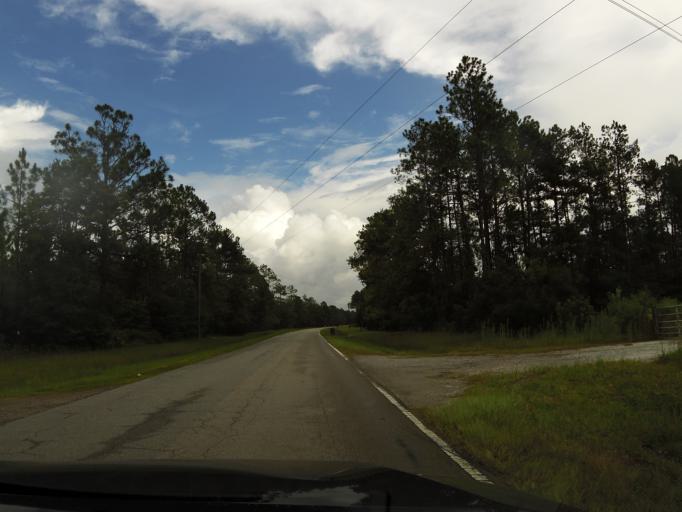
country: US
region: Florida
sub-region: Duval County
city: Baldwin
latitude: 30.3959
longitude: -81.9505
